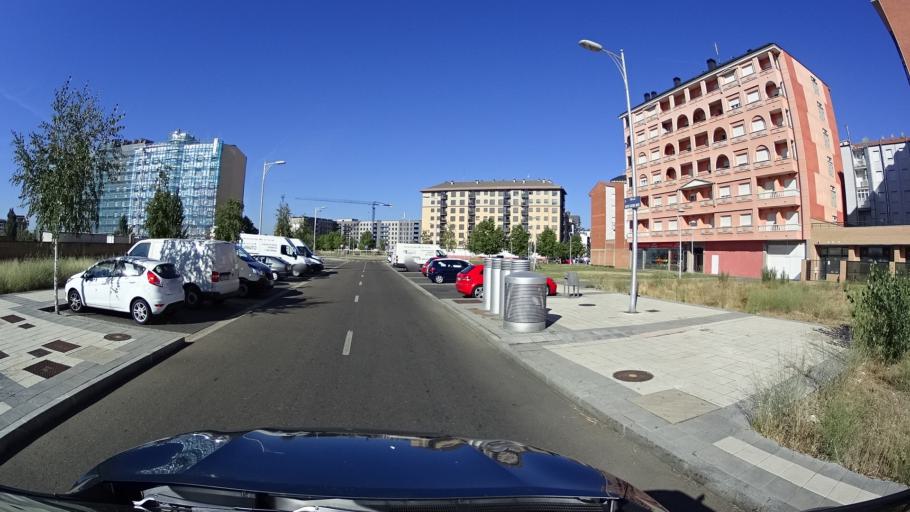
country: ES
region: Castille and Leon
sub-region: Provincia de Leon
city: Leon
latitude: 42.5865
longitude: -5.5602
